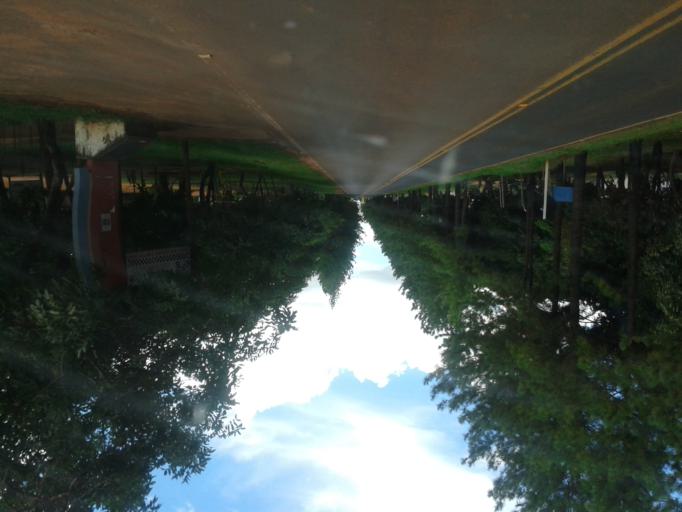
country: BR
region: Minas Gerais
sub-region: Santa Vitoria
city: Santa Vitoria
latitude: -18.8561
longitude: -50.1298
